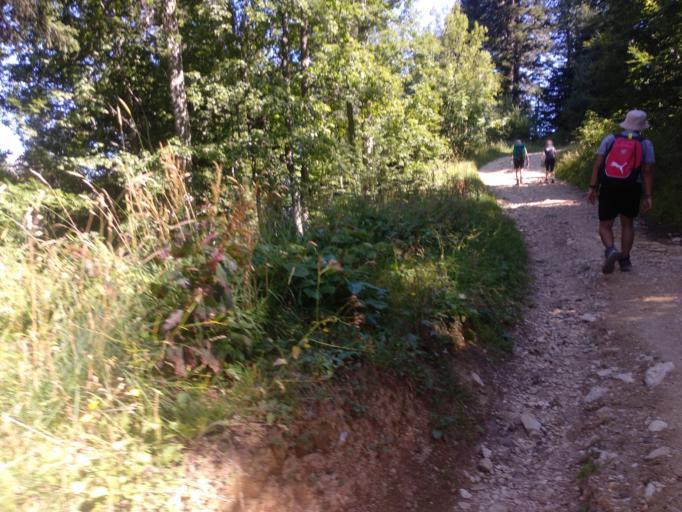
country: FR
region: Rhone-Alpes
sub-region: Departement de l'Isere
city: Le Sappey-en-Chartreuse
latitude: 45.2910
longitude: 5.7763
